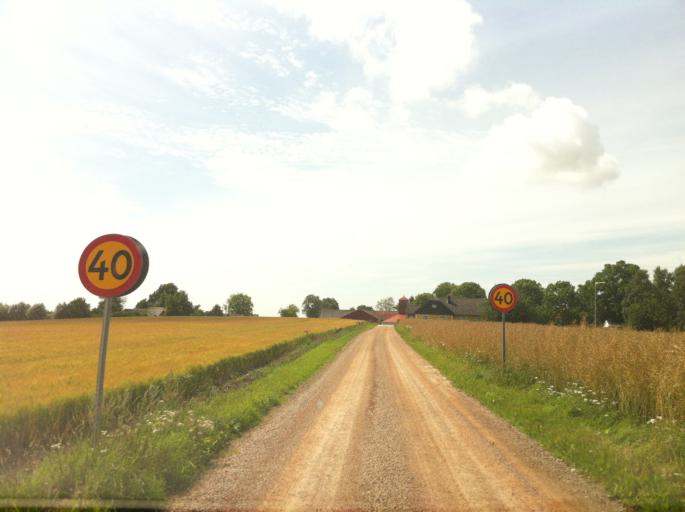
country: SE
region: Skane
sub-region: Skurups Kommun
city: Skurup
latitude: 55.4523
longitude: 13.4314
